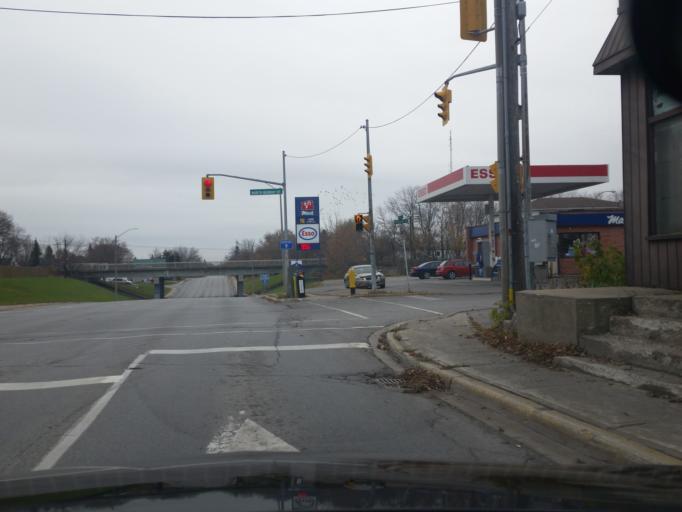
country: CA
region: Ontario
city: Quinte West
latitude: 44.1193
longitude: -77.5767
